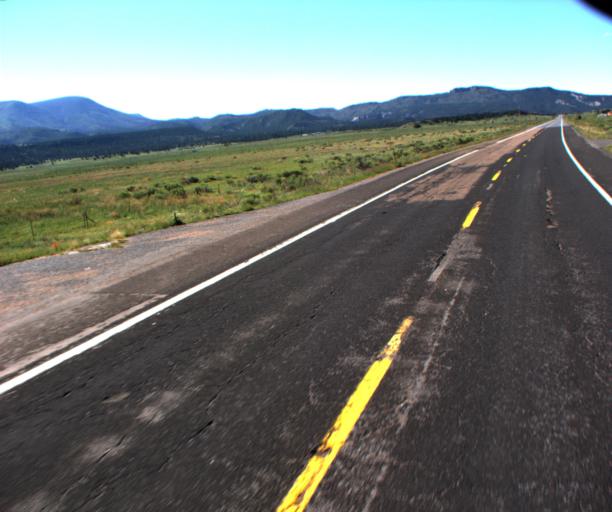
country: US
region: Arizona
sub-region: Apache County
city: Eagar
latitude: 34.0253
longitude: -109.1836
